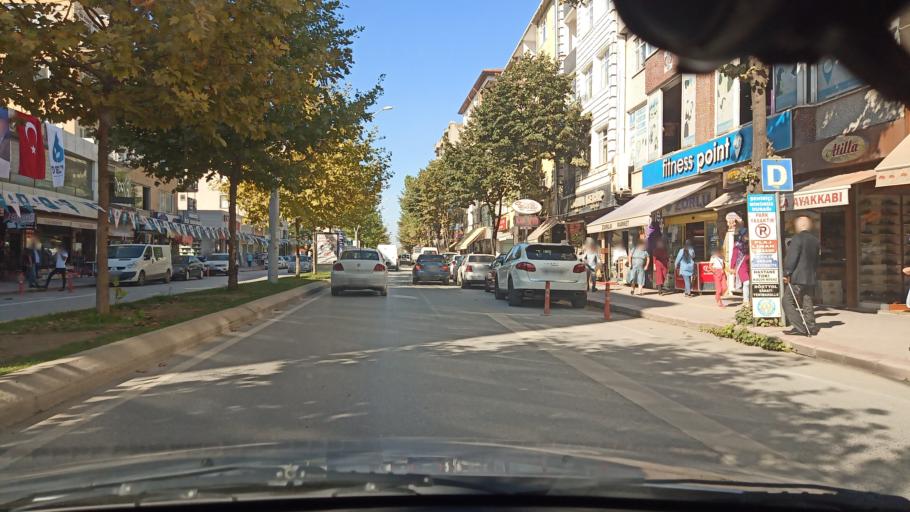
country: TR
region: Sakarya
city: Karasu
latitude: 41.0960
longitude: 30.6924
